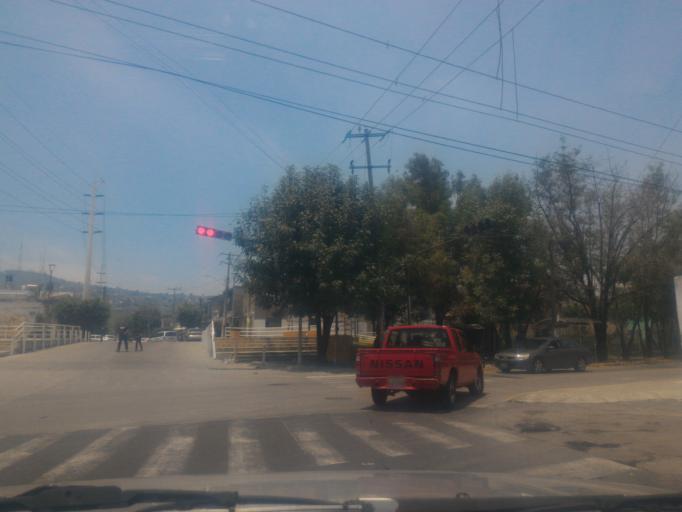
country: MX
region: Jalisco
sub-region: Tlajomulco de Zuniga
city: Altus Bosques
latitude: 20.6205
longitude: -103.3639
